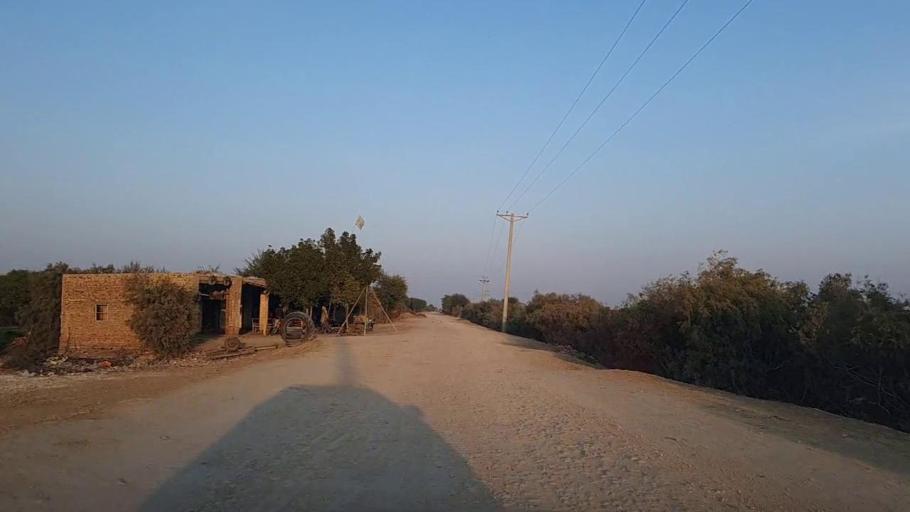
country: PK
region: Sindh
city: Tando Mittha Khan
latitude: 25.9674
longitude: 69.0772
